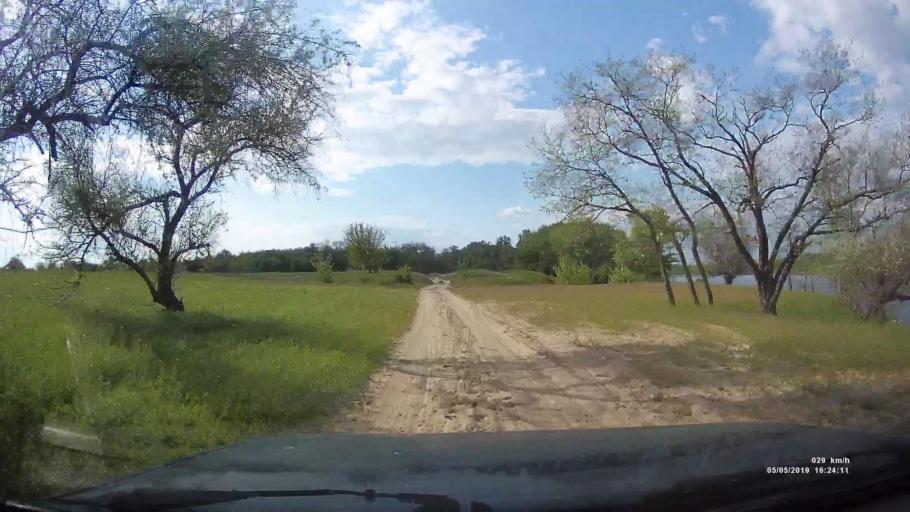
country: RU
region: Rostov
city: Konstantinovsk
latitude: 47.7586
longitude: 41.0271
